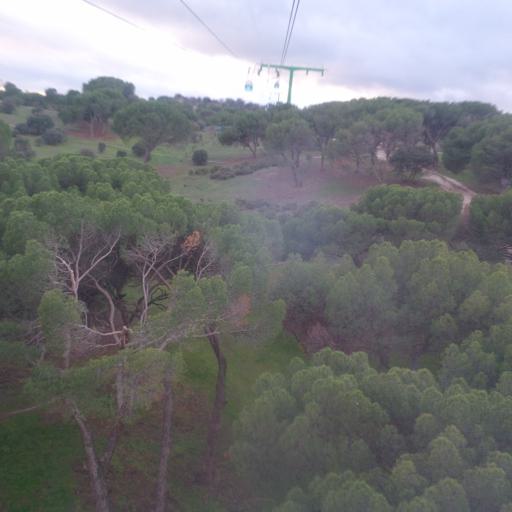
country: ES
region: Madrid
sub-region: Provincia de Madrid
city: Moncloa-Aravaca
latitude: 40.4242
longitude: -3.7342
